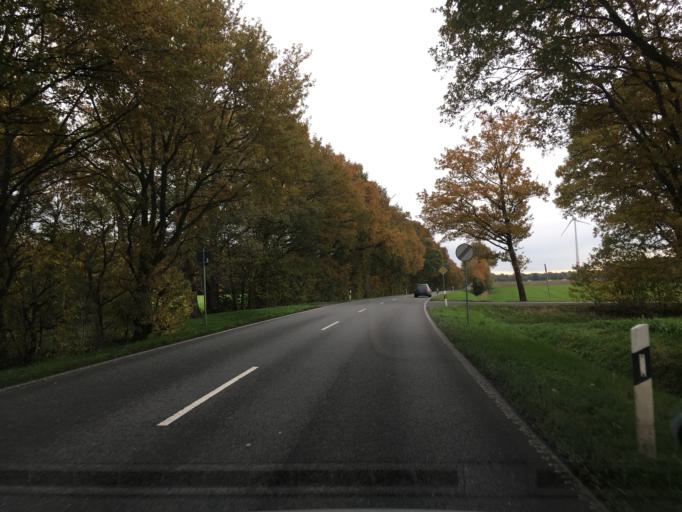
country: DE
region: North Rhine-Westphalia
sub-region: Regierungsbezirk Munster
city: Heiden
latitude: 51.7964
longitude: 6.9565
